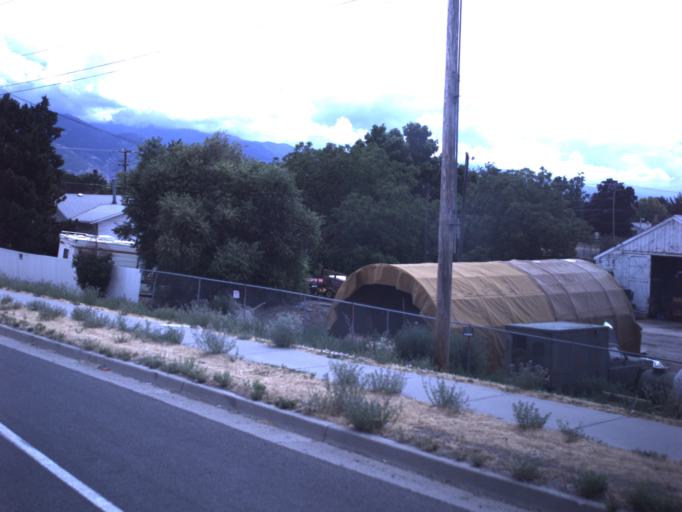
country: US
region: Utah
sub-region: Davis County
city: Clearfield
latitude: 41.0890
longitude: -112.0079
